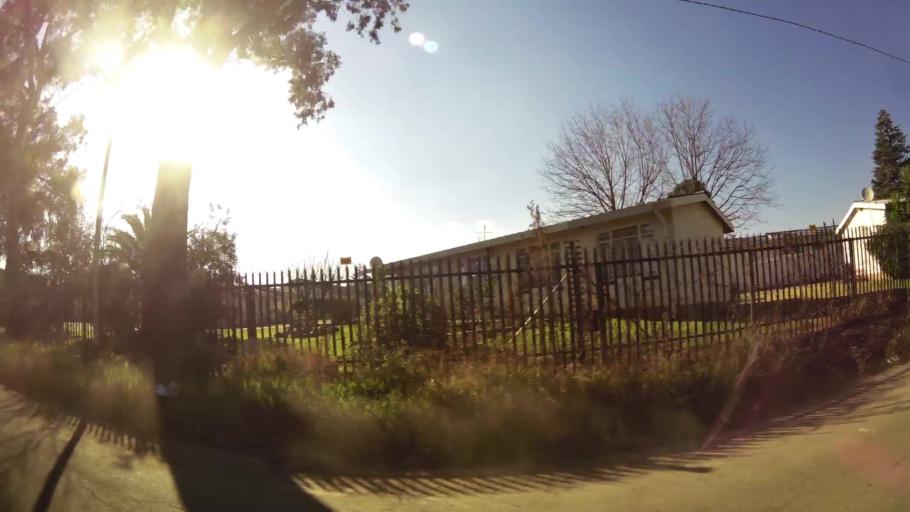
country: ZA
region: Gauteng
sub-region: City of Johannesburg Metropolitan Municipality
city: Roodepoort
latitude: -26.1593
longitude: 27.8578
